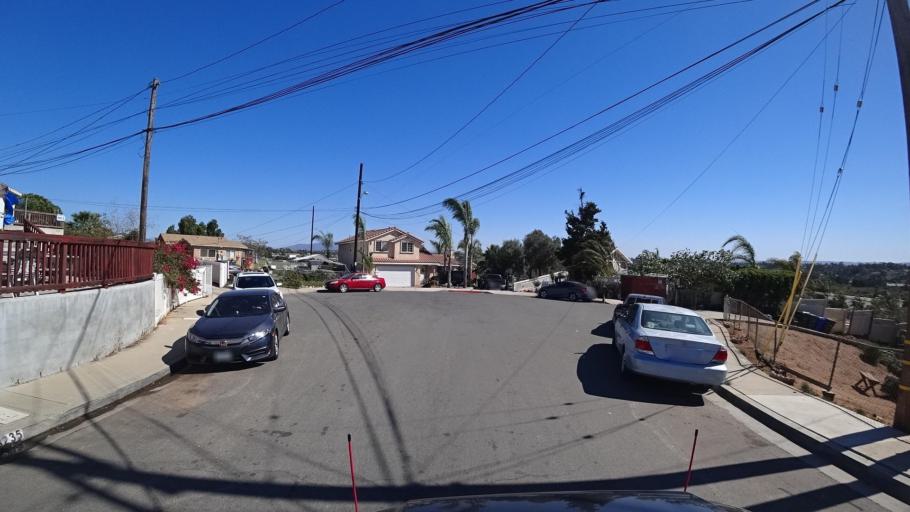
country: US
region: California
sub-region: San Diego County
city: Chula Vista
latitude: 32.6622
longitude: -117.0690
